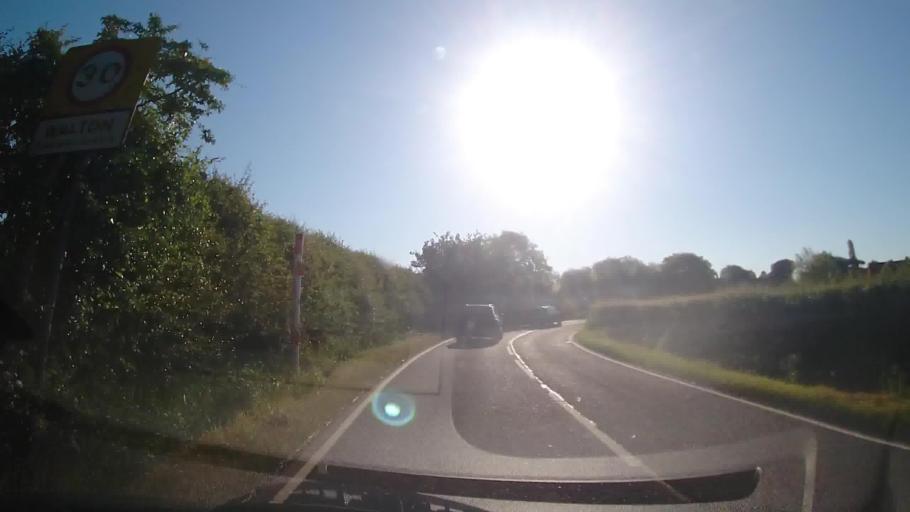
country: GB
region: England
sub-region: Shropshire
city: Shawbury
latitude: 52.7634
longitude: -2.6146
